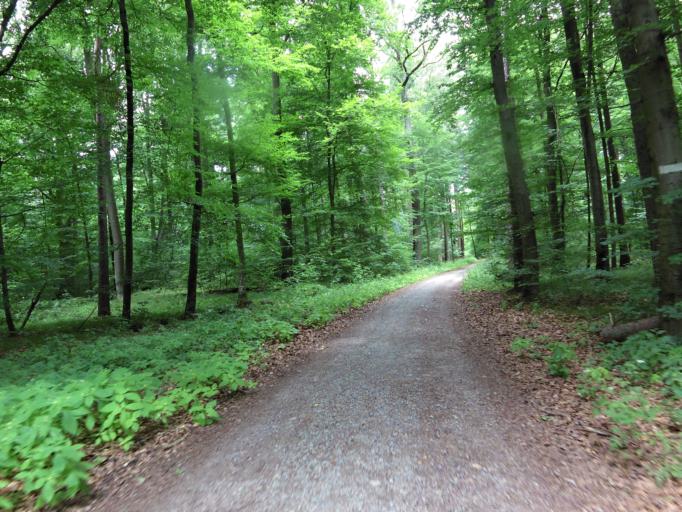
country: DE
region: Bavaria
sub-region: Regierungsbezirk Unterfranken
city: Reichenberg
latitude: 49.7592
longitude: 9.9092
